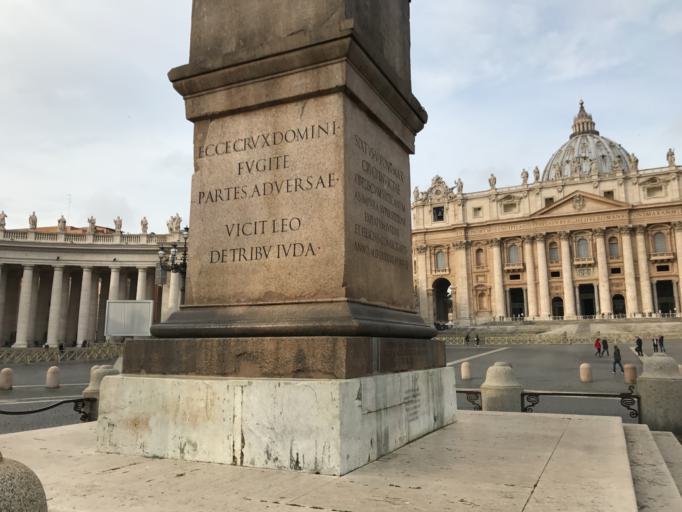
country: VA
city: Vatican City
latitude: 41.9023
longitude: 12.4574
